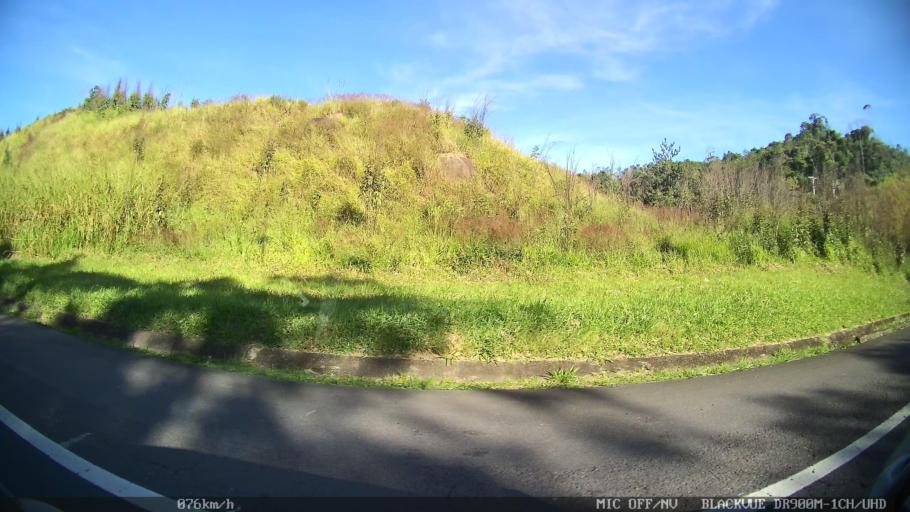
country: BR
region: Parana
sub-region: Antonina
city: Antonina
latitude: -25.0362
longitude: -48.5410
